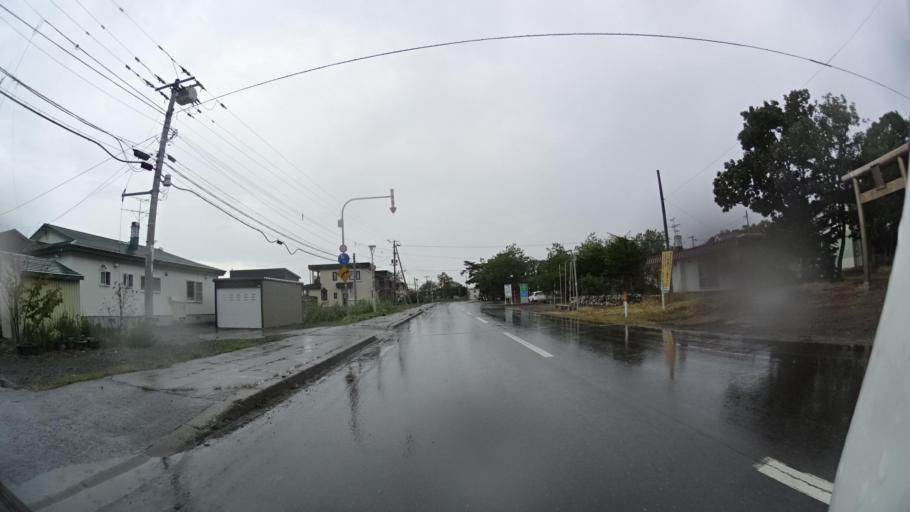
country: JP
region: Hokkaido
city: Mombetsu
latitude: 44.3245
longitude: 143.5014
